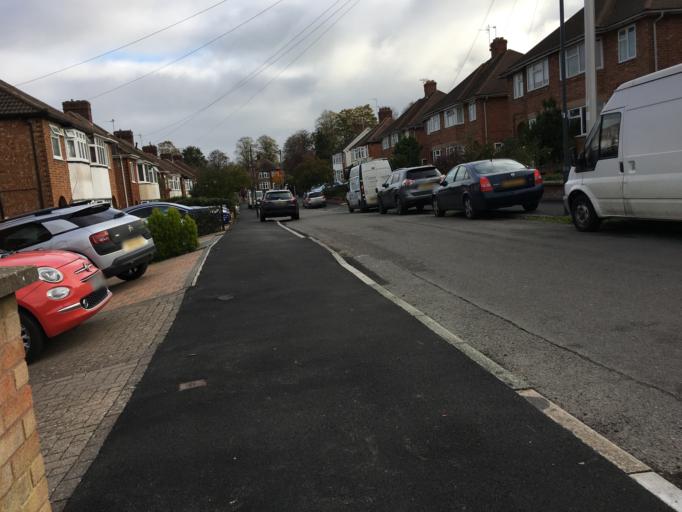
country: GB
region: England
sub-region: Warwickshire
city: Rugby
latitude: 52.3626
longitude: -1.2651
